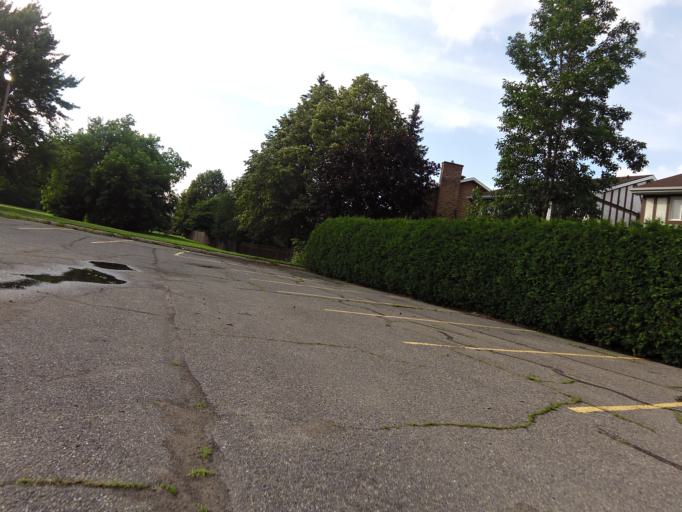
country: CA
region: Ontario
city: Bells Corners
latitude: 45.3263
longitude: -75.7739
